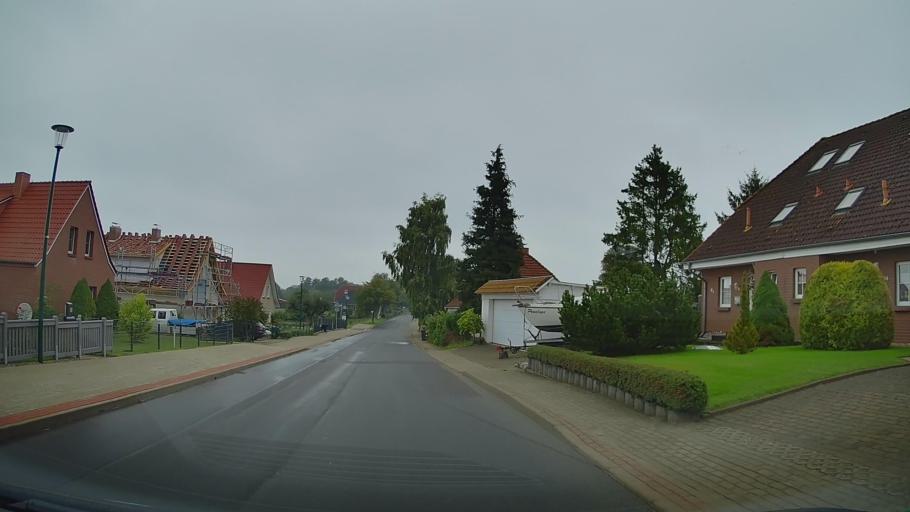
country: DE
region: Mecklenburg-Vorpommern
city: Gramkow
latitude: 53.9284
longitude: 11.3279
